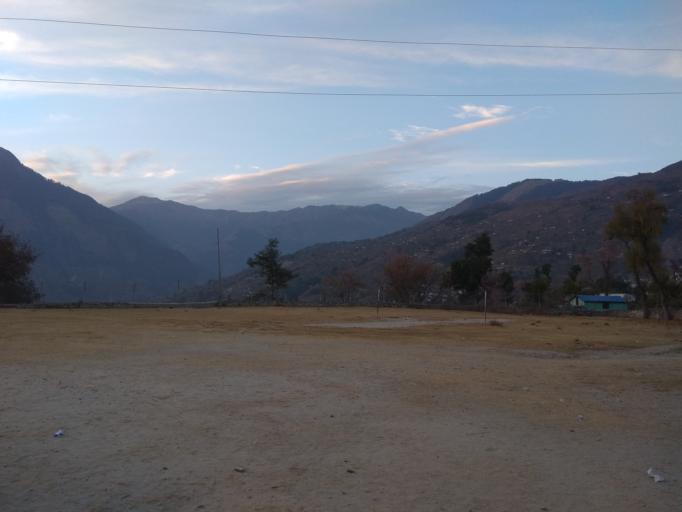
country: NP
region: Far Western
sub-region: Seti Zone
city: Achham
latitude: 29.2422
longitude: 81.6421
